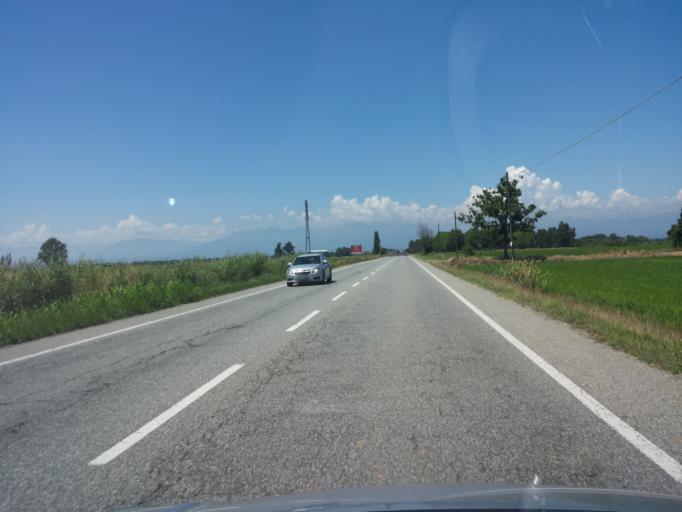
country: IT
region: Piedmont
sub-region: Provincia di Vercelli
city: Formigliana
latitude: 45.4192
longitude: 8.3092
